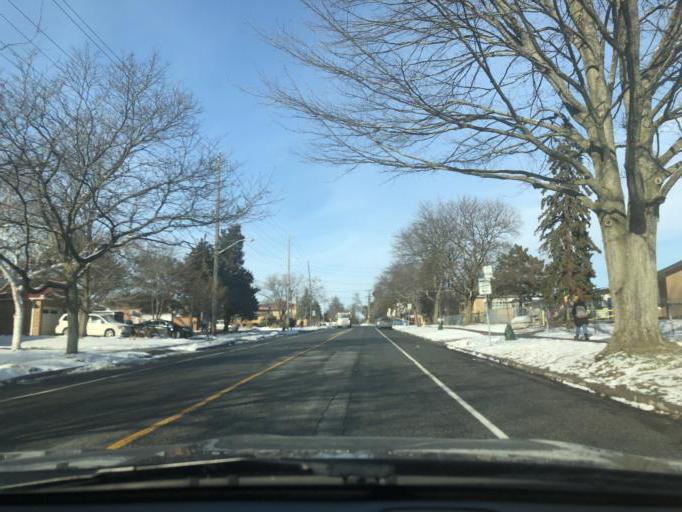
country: CA
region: Ontario
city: Scarborough
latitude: 43.7860
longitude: -79.1501
